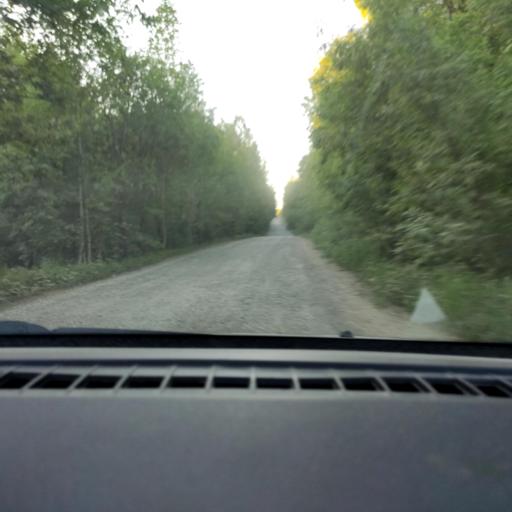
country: RU
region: Perm
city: Polazna
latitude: 58.1245
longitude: 56.4362
